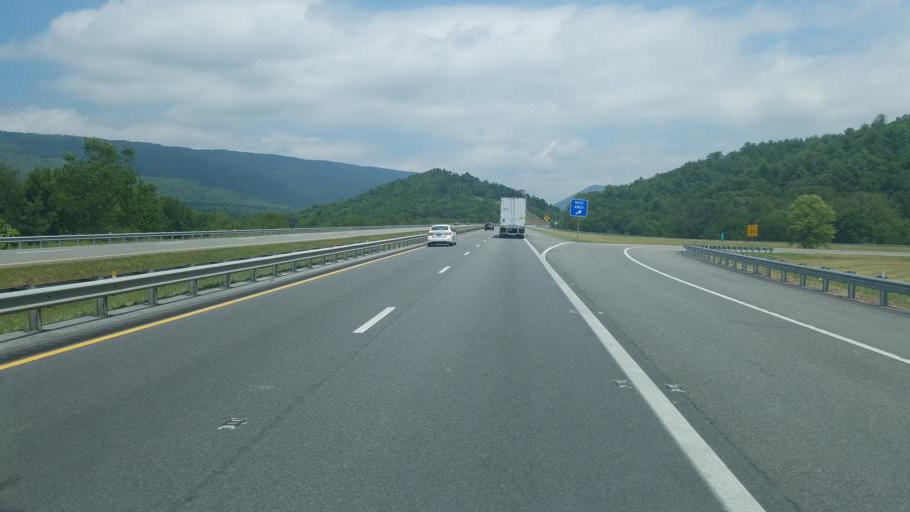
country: US
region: Virginia
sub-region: Bland County
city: Bland
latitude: 37.1866
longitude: -81.1307
